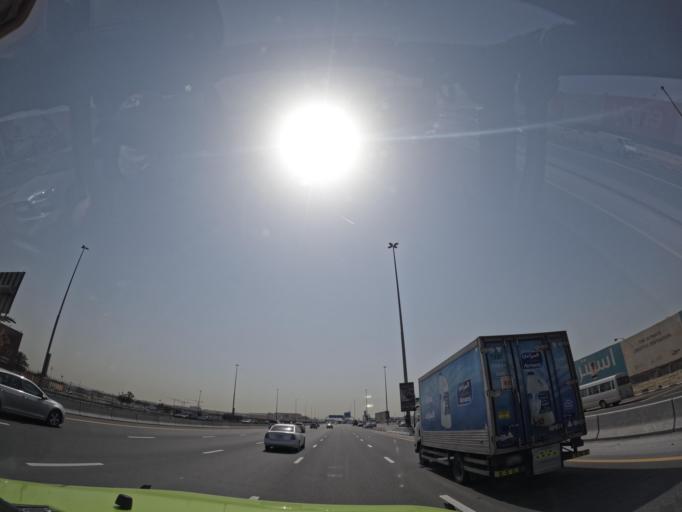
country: AE
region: Ash Shariqah
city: Sharjah
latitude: 25.3270
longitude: 55.4606
